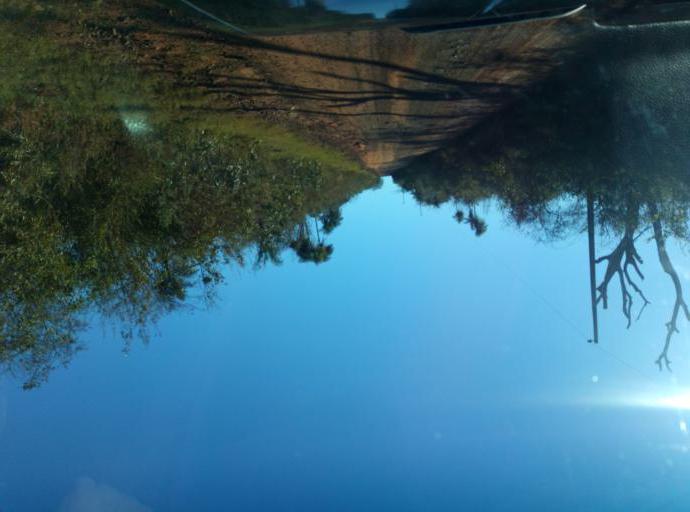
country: PY
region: Caaguazu
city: Carayao
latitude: -25.1577
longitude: -56.2970
